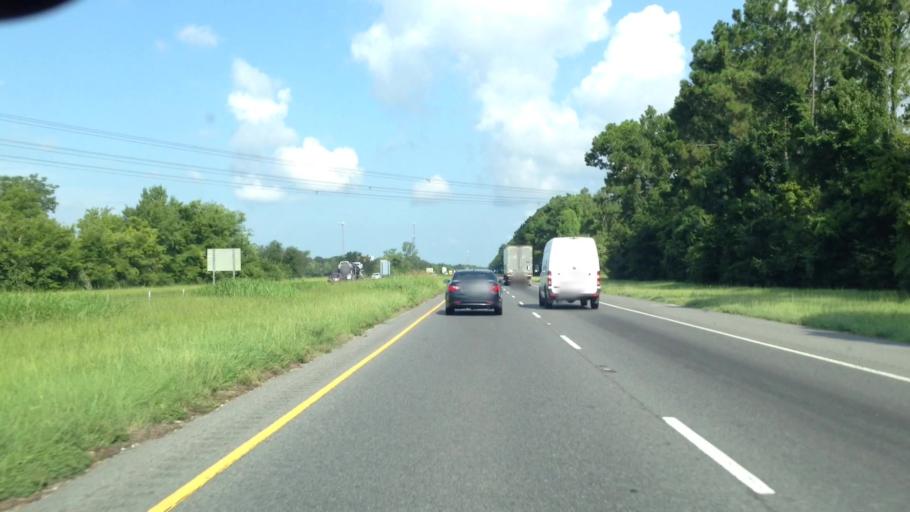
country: US
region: Louisiana
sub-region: Saint John the Baptist Parish
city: Laplace
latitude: 30.0915
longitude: -90.4518
